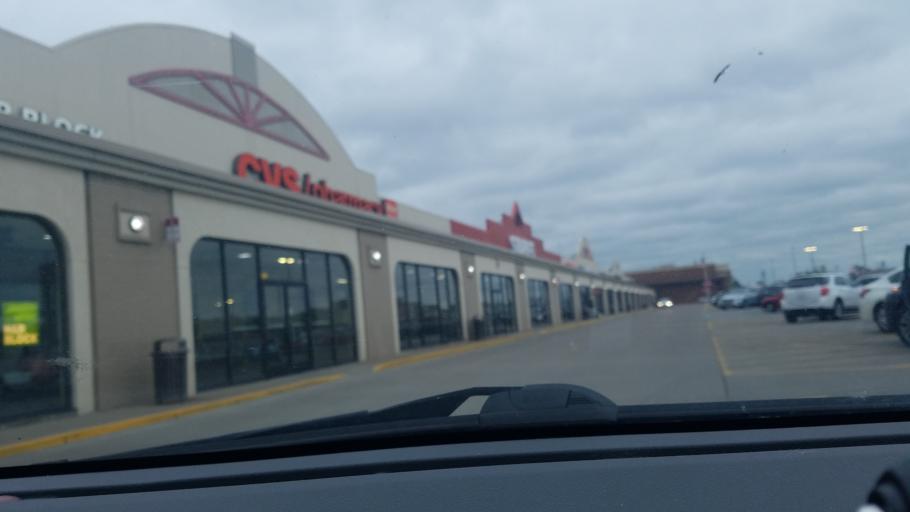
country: US
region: Michigan
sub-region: Wayne County
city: Dearborn Heights
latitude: 42.3017
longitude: -83.2594
